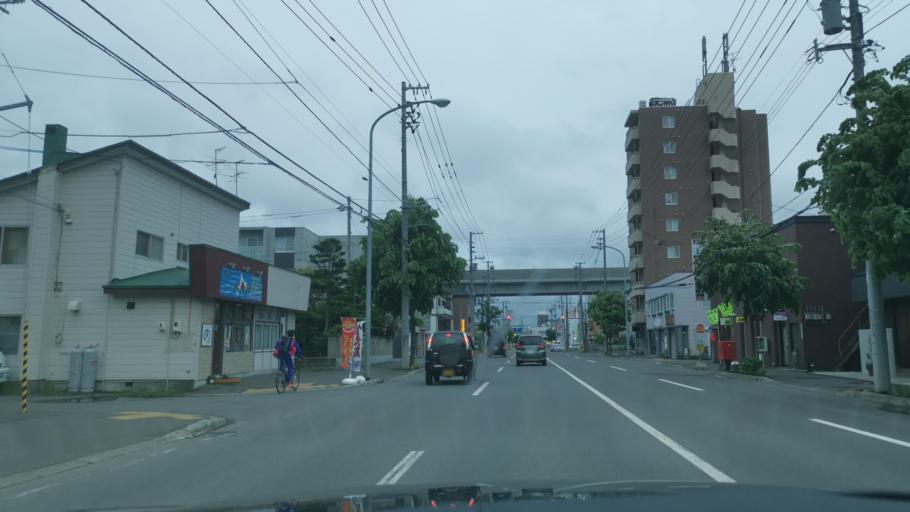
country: JP
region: Hokkaido
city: Sapporo
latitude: 43.1034
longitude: 141.3257
